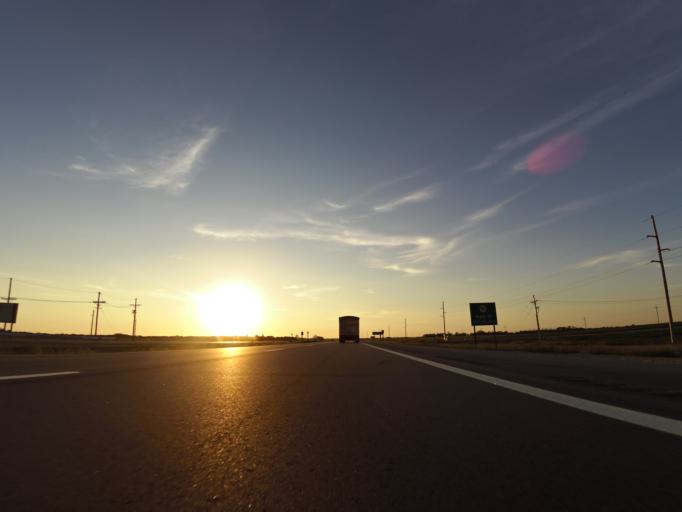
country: US
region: Kansas
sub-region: Reno County
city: South Hutchinson
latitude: 38.0133
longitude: -97.9596
